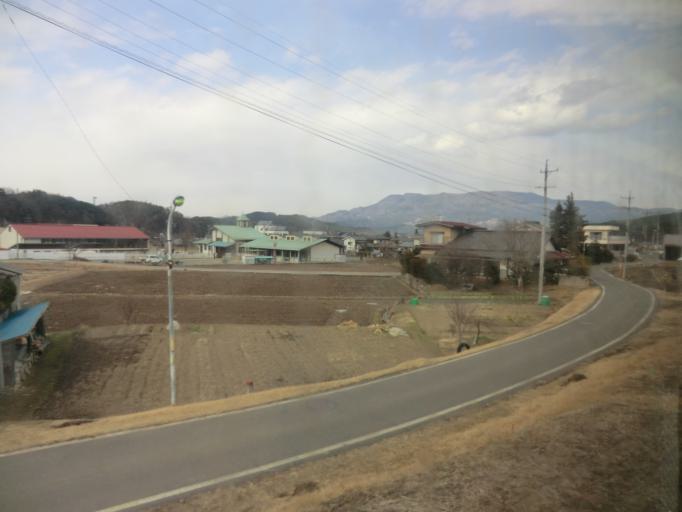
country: JP
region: Nagano
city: Hotaka
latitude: 36.4022
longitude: 138.0140
